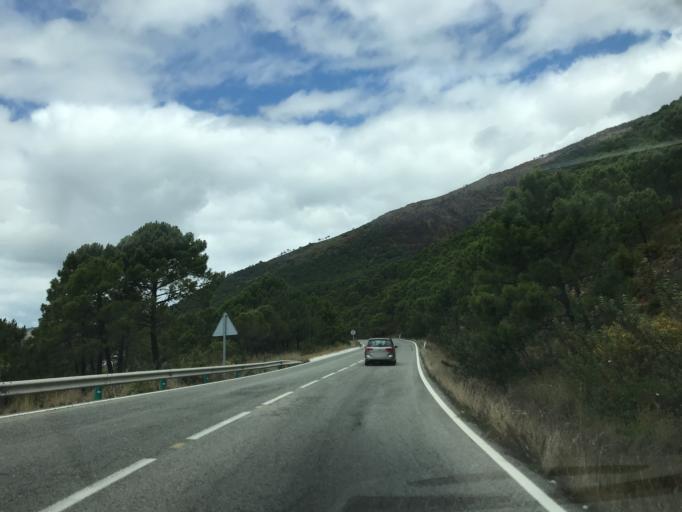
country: ES
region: Andalusia
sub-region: Provincia de Malaga
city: Benahavis
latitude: 36.5549
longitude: -5.0411
